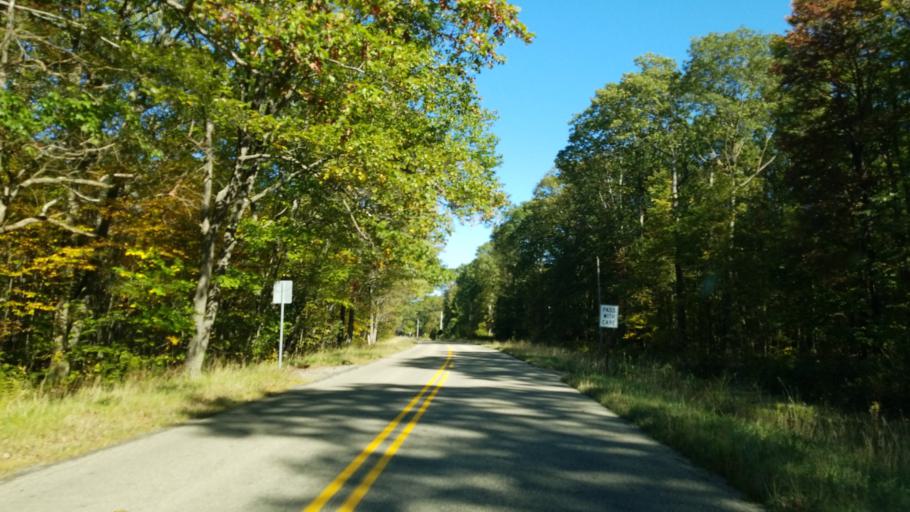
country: US
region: Pennsylvania
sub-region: Clearfield County
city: Shiloh
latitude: 41.2505
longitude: -78.3430
